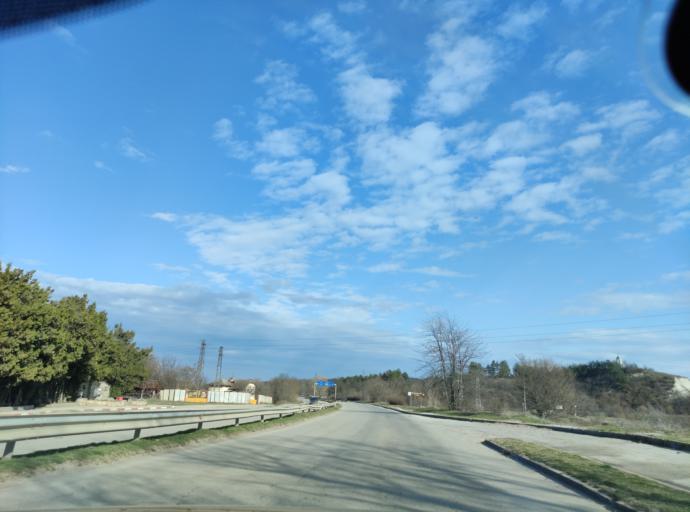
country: BG
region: Pleven
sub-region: Obshtina Dolna Mitropoliya
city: Dolna Mitropoliya
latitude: 43.4329
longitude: 24.5457
